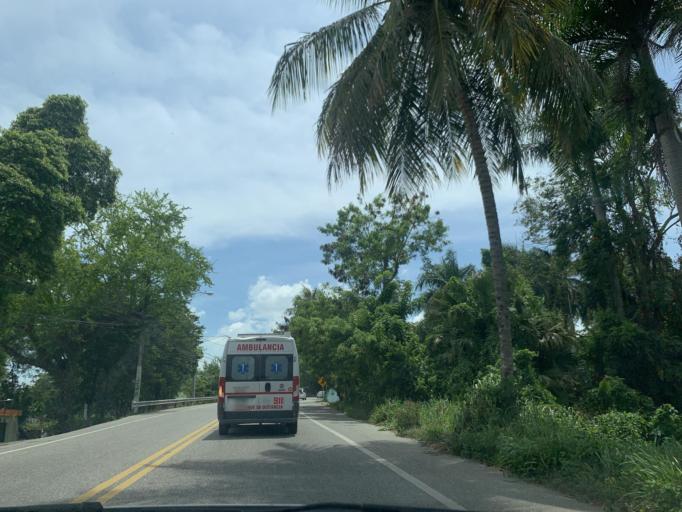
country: DO
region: Puerto Plata
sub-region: Puerto Plata
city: Puerto Plata
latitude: 19.7205
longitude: -70.6179
